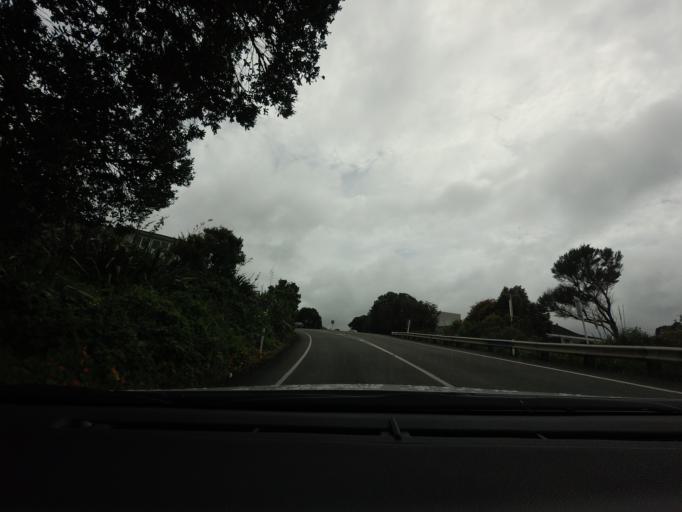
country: NZ
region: Auckland
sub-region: Auckland
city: Rothesay Bay
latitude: -36.5720
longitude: 174.6934
